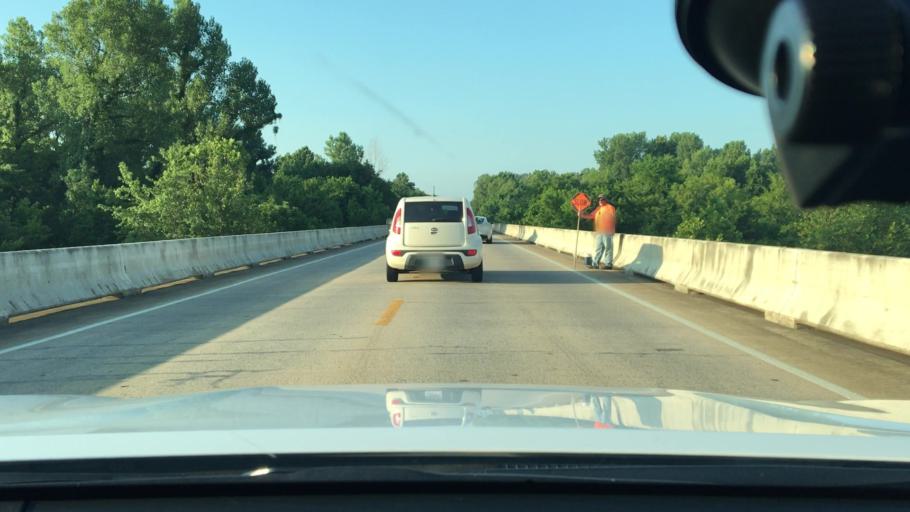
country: US
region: Arkansas
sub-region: Johnson County
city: Clarksville
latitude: 35.4052
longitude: -93.5315
